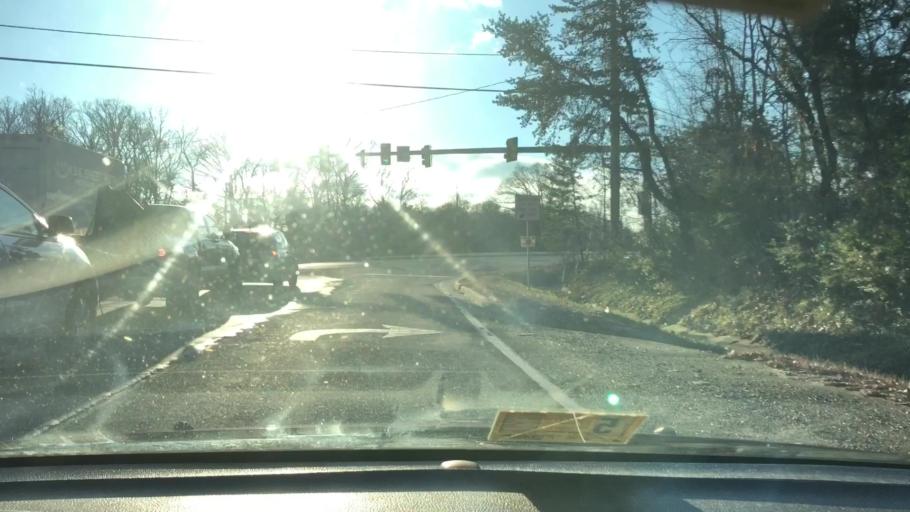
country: US
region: Virginia
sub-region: Fairfax County
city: Franconia
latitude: 38.7940
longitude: -77.1375
